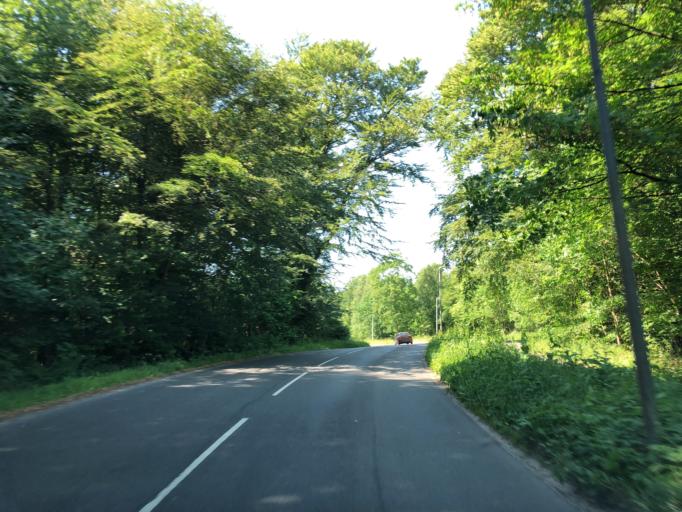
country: DK
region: South Denmark
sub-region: Kolding Kommune
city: Kolding
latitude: 55.5114
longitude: 9.4932
